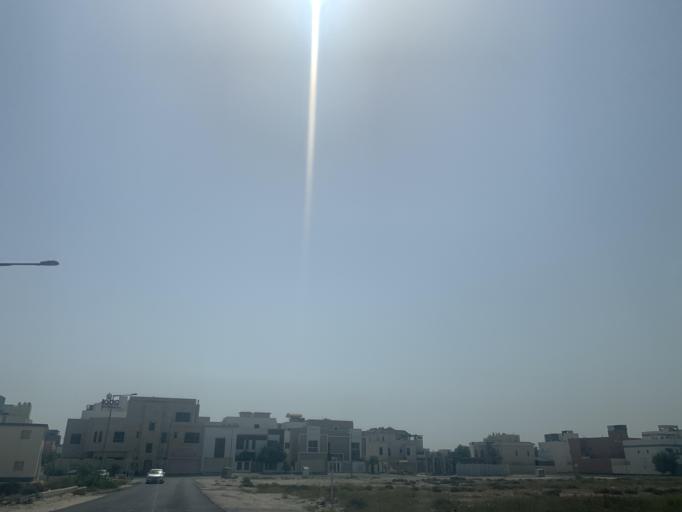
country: BH
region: Manama
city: Jidd Hafs
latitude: 26.2062
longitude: 50.4633
